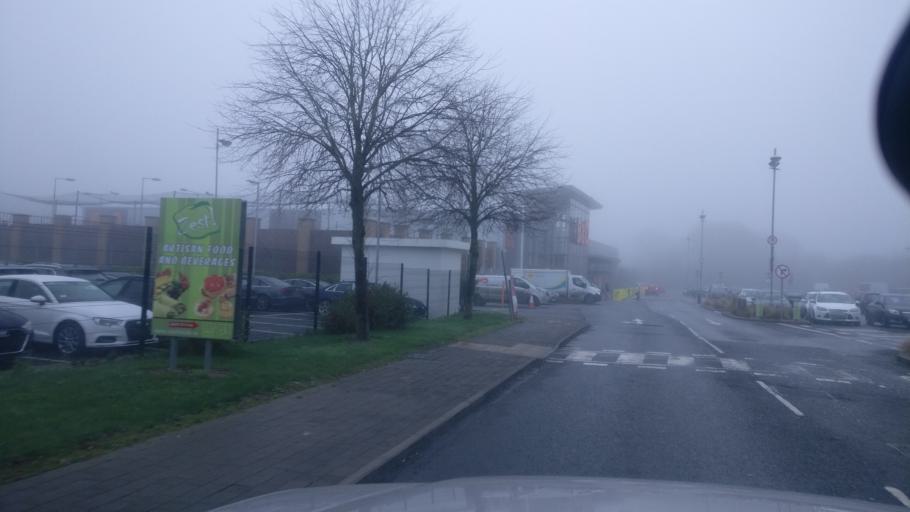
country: IE
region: Munster
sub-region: County Limerick
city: Annacotty
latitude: 52.6494
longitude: -8.5756
